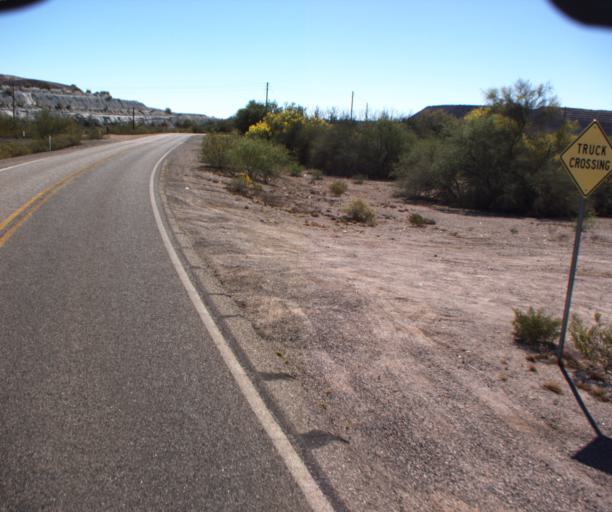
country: US
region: Arizona
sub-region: Pima County
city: Ajo
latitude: 32.3724
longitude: -112.8578
